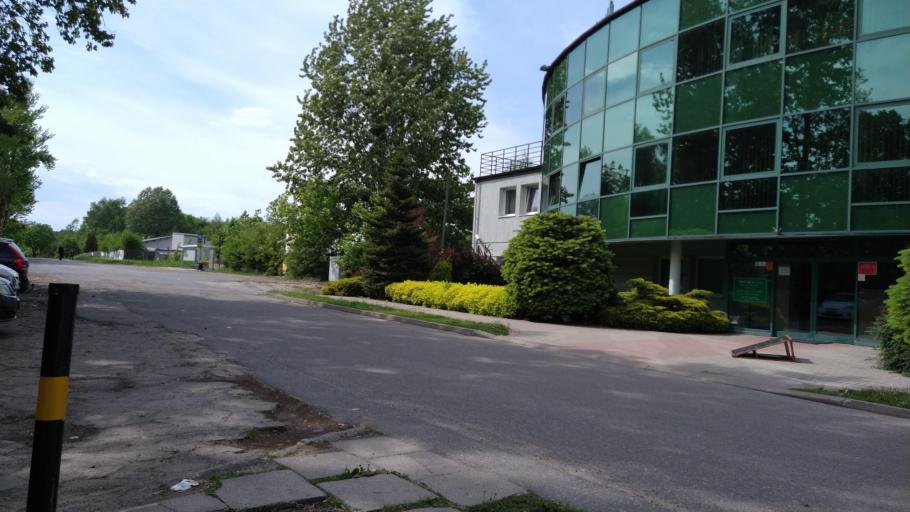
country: PL
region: Warmian-Masurian Voivodeship
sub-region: Powiat olsztynski
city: Olsztyn
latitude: 53.7958
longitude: 20.5402
